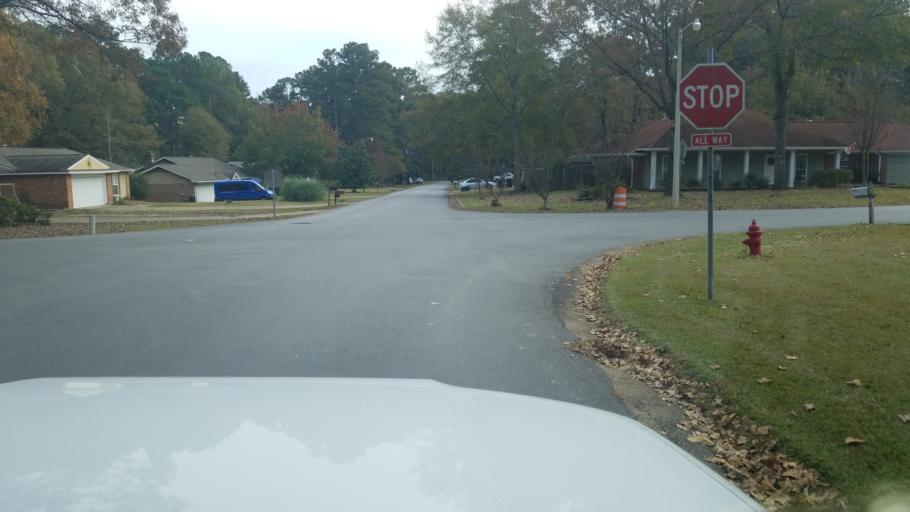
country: US
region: Mississippi
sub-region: Madison County
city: Ridgeland
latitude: 32.3854
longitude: -90.0335
